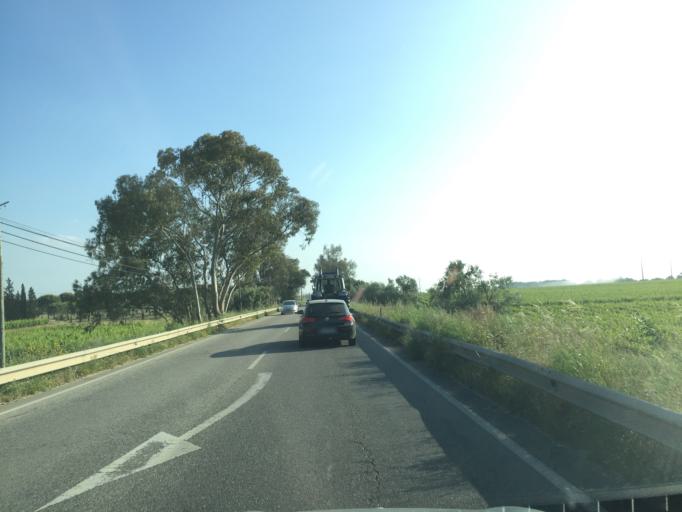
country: PT
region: Santarem
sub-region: Almeirim
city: Almeirim
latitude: 39.1971
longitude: -8.6422
